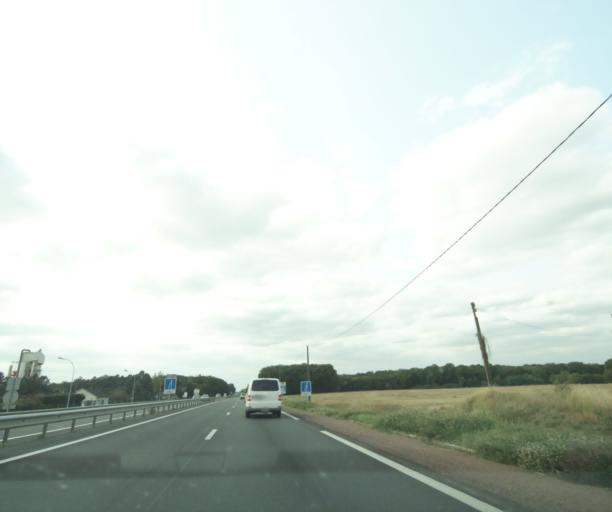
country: FR
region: Centre
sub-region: Departement d'Indre-et-Loire
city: Esvres
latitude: 47.3025
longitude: 0.7948
